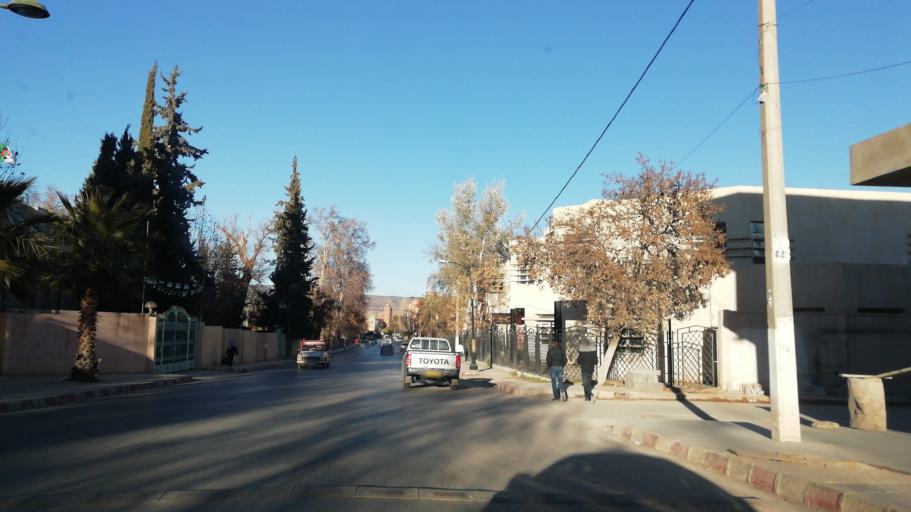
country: DZ
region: Tlemcen
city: Sebdou
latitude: 34.6416
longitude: -1.3283
